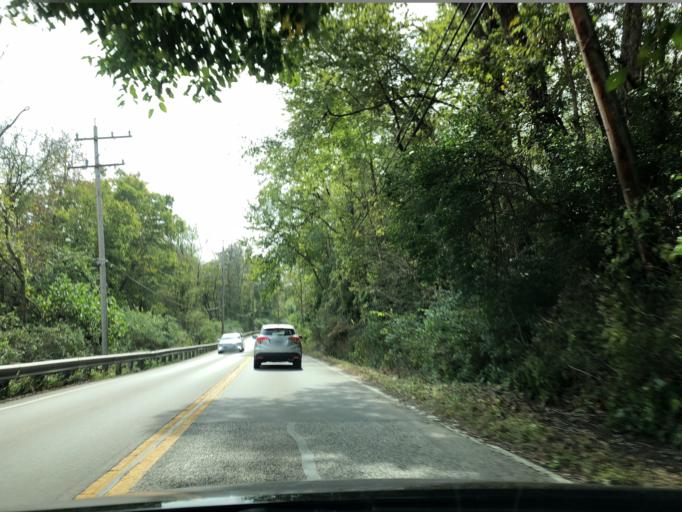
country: US
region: Ohio
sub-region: Clermont County
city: Milford
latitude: 39.1841
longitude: -84.2926
